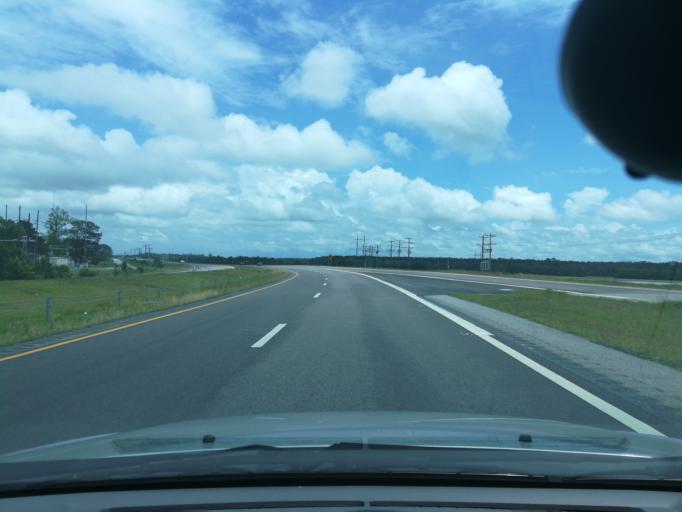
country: US
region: North Carolina
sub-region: Tyrrell County
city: Columbia
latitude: 35.8754
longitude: -76.3852
